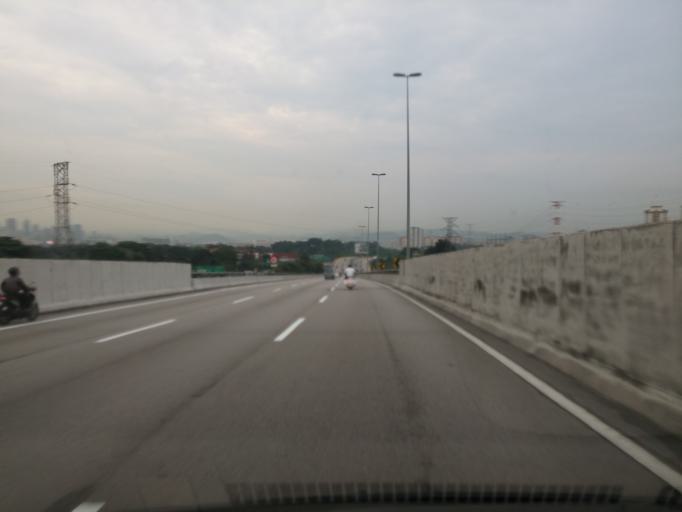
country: MY
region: Kuala Lumpur
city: Kuala Lumpur
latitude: 3.1005
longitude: 101.7025
